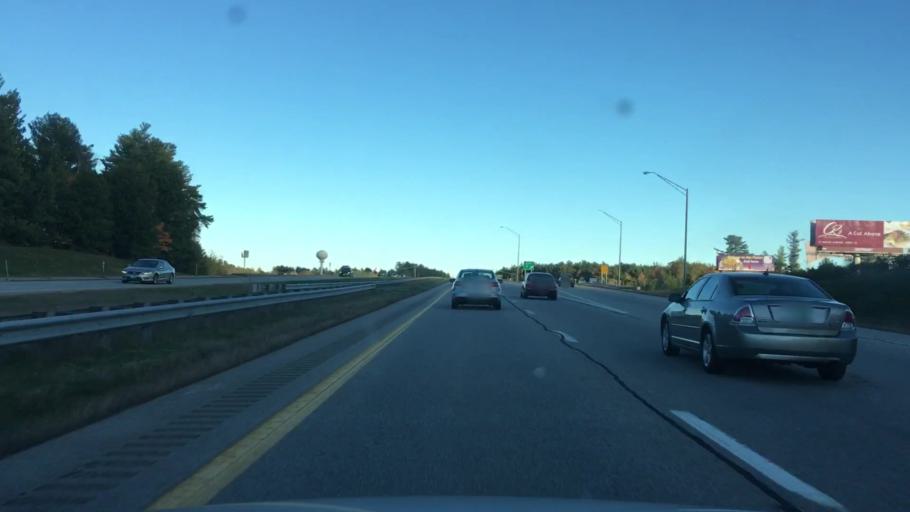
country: US
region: New Hampshire
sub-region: Rockingham County
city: Epping
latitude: 43.0272
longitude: -71.0795
